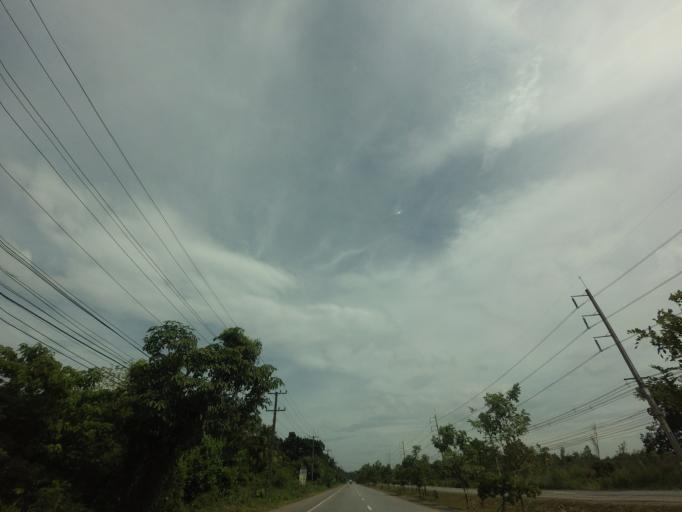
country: TH
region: Rayong
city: Klaeng
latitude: 12.6949
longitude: 101.5386
